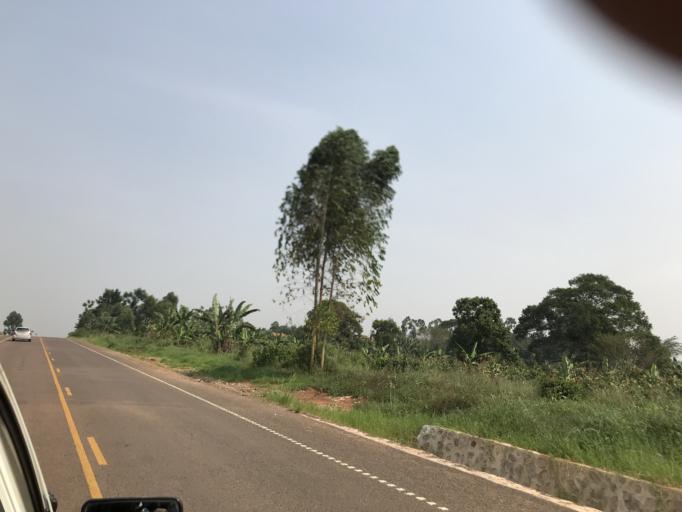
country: UG
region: Central Region
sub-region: Kalungu District
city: Kalungu
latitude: -0.2284
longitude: 31.7330
